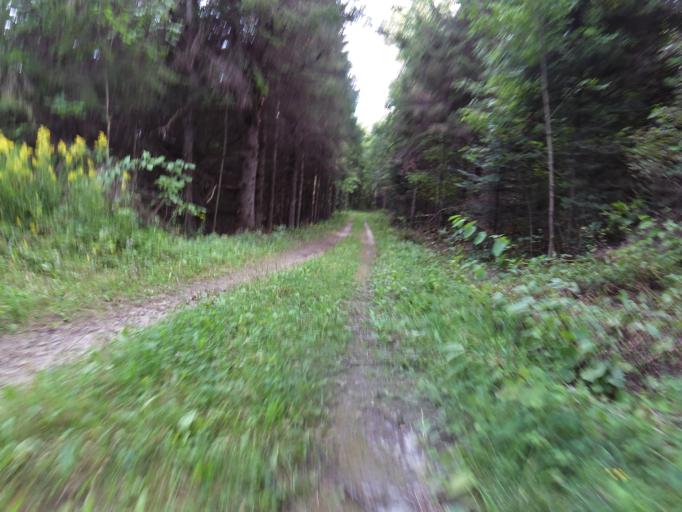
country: CA
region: Quebec
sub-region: Outaouais
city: Wakefield
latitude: 45.6405
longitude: -75.9948
